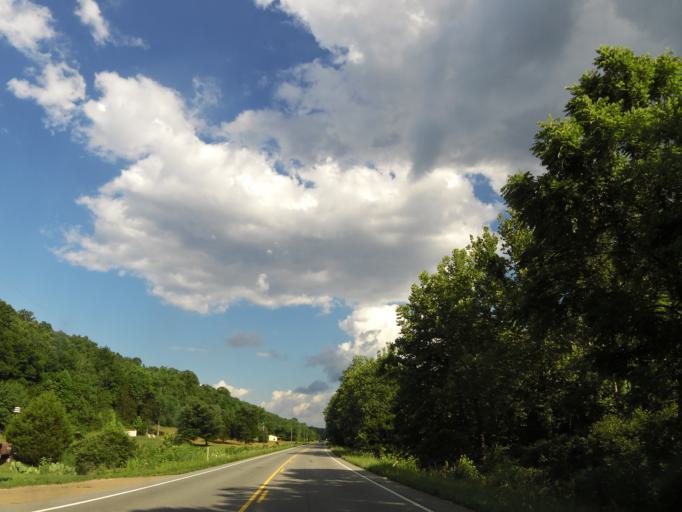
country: US
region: Tennessee
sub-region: Perry County
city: Linden
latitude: 35.5971
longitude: -87.6972
